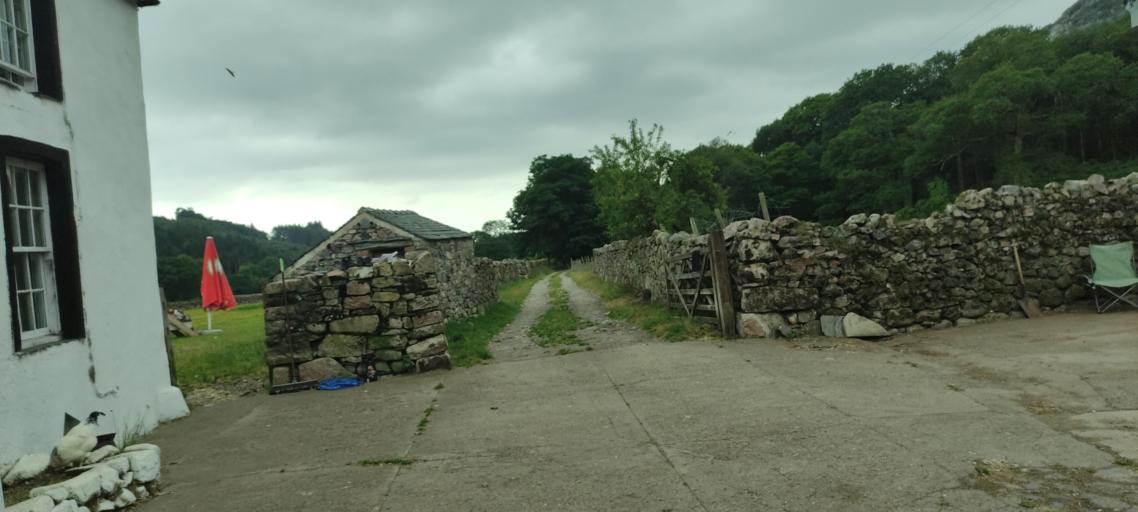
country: GB
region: England
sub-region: Cumbria
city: Seascale
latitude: 54.4042
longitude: -3.3047
